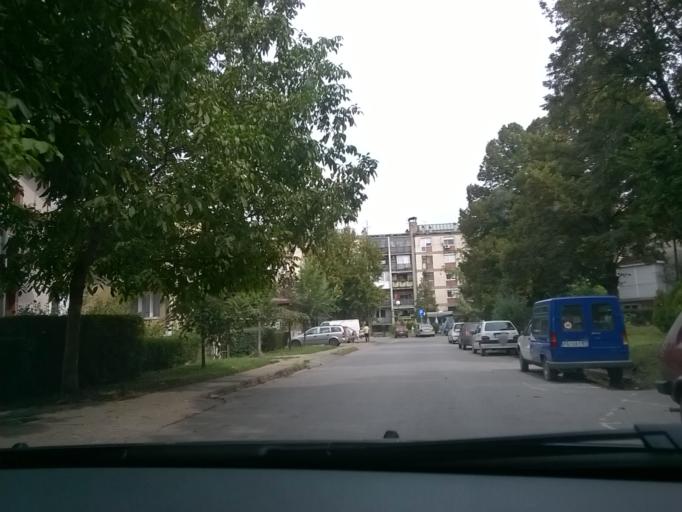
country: RS
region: Autonomna Pokrajina Vojvodina
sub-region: Juznobanatski Okrug
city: Pancevo
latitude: 44.8799
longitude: 20.6521
